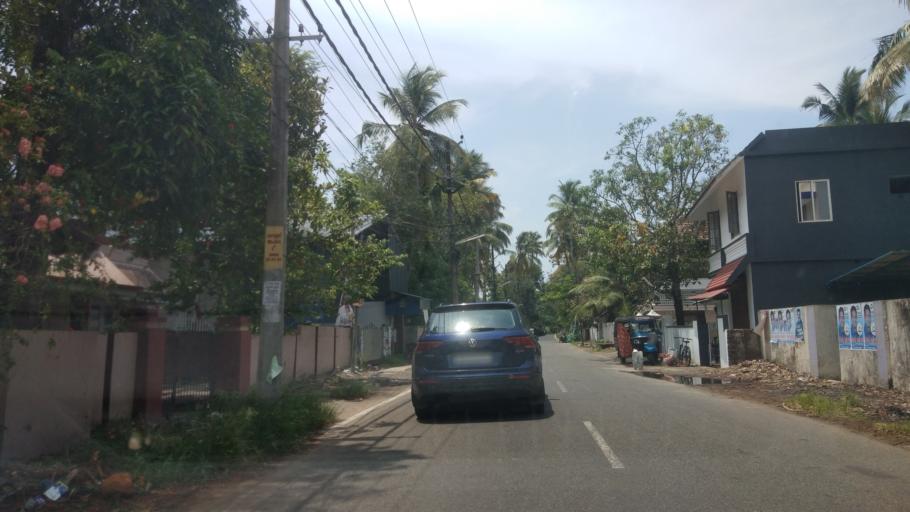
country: IN
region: Kerala
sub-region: Ernakulam
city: Cochin
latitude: 9.8963
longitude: 76.2583
